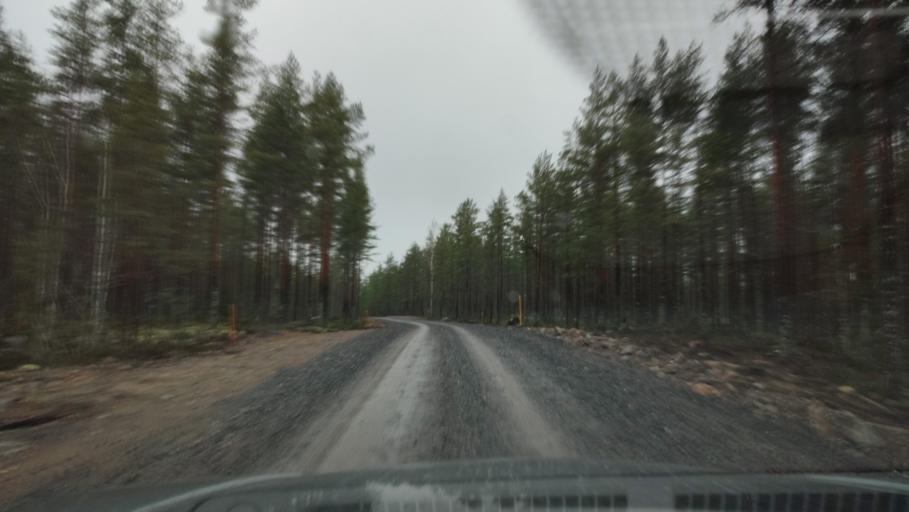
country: FI
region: Southern Ostrobothnia
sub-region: Suupohja
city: Karijoki
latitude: 62.1561
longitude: 21.6170
